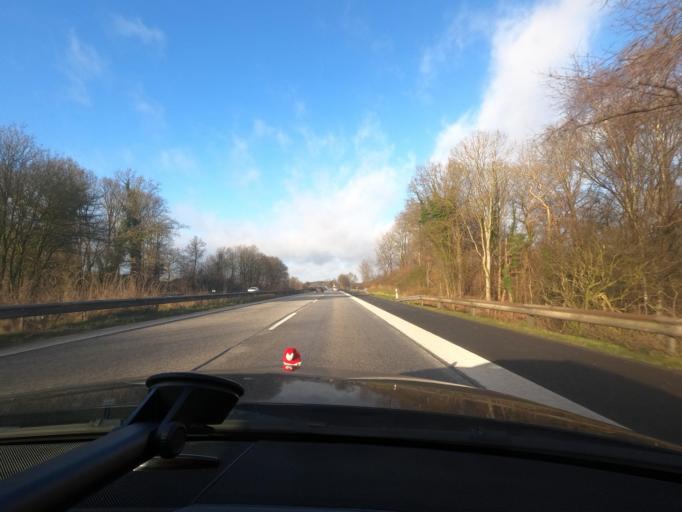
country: DE
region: Schleswig-Holstein
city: Alt Duvenstedt
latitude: 54.3874
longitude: 9.6539
